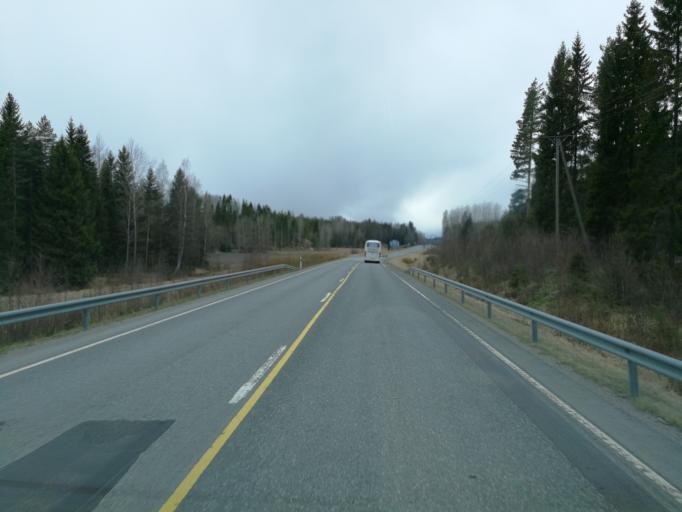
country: FI
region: Varsinais-Suomi
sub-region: Salo
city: Muurla
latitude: 60.3687
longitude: 23.3426
